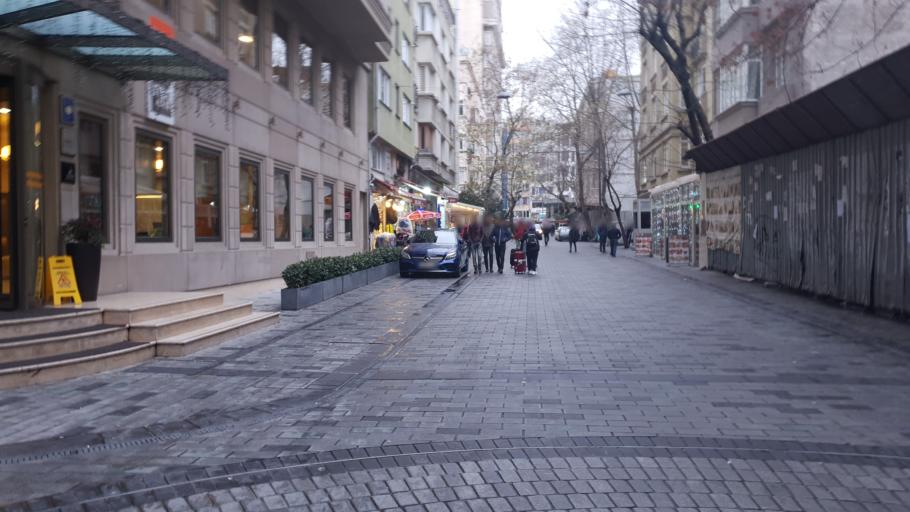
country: TR
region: Istanbul
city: Sisli
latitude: 41.0391
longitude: 28.9852
